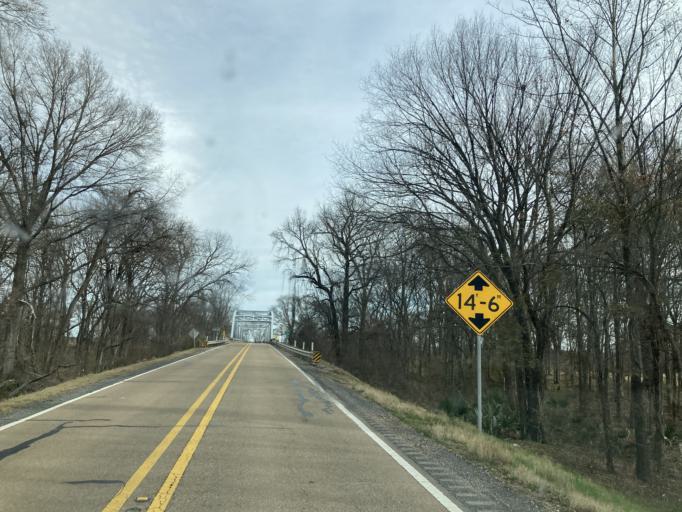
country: US
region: Mississippi
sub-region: Washington County
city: Hollandale
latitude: 33.1836
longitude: -90.6880
